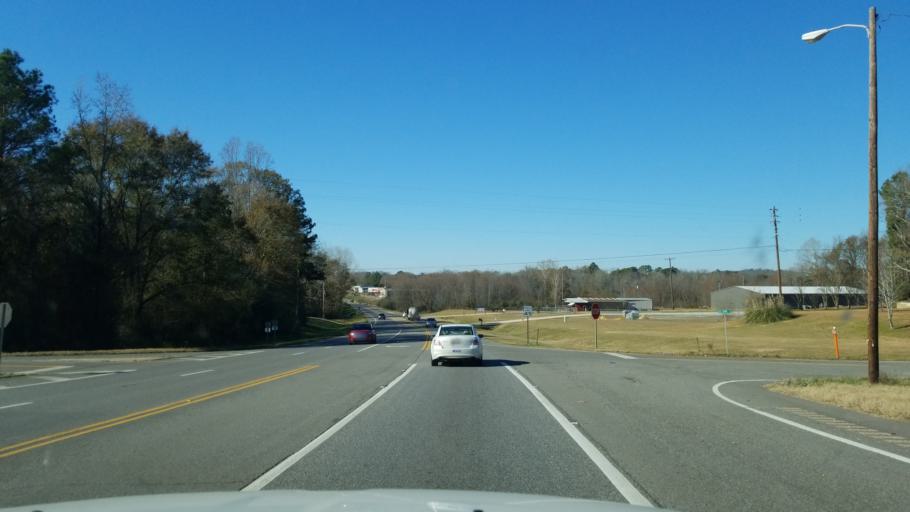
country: US
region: Alabama
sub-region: Pickens County
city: Gordo
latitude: 33.3132
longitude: -87.8939
